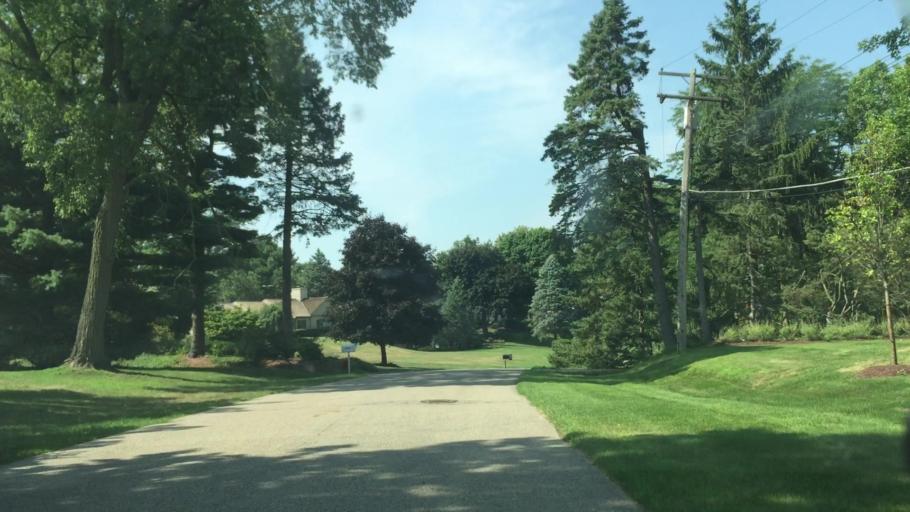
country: US
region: Michigan
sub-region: Oakland County
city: Franklin
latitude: 42.5388
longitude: -83.3162
